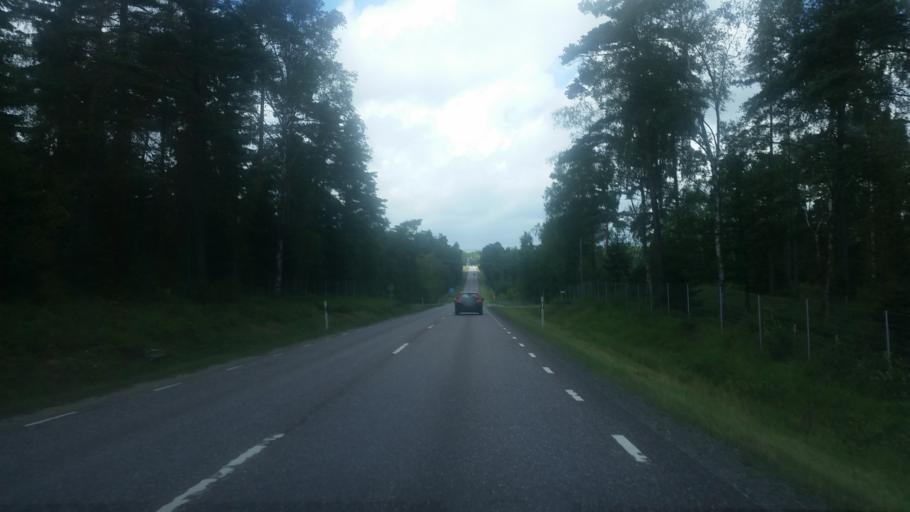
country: SE
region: Vaestra Goetaland
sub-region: Partille Kommun
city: Furulund
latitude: 57.6969
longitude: 12.1561
